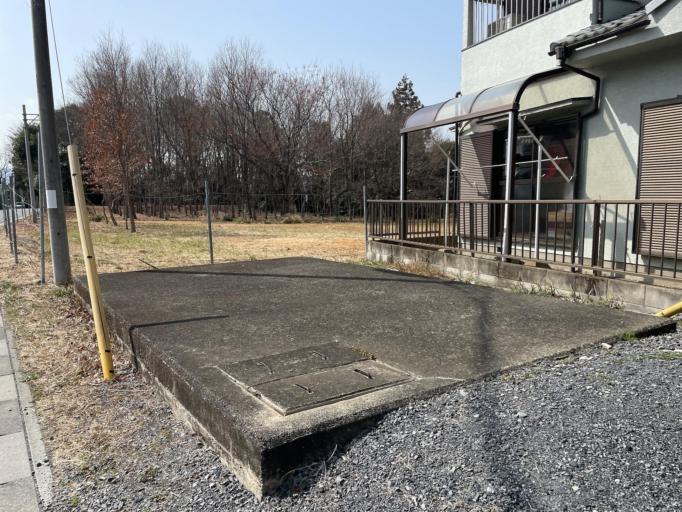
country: JP
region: Saitama
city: Yorii
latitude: 36.1090
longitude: 139.2505
